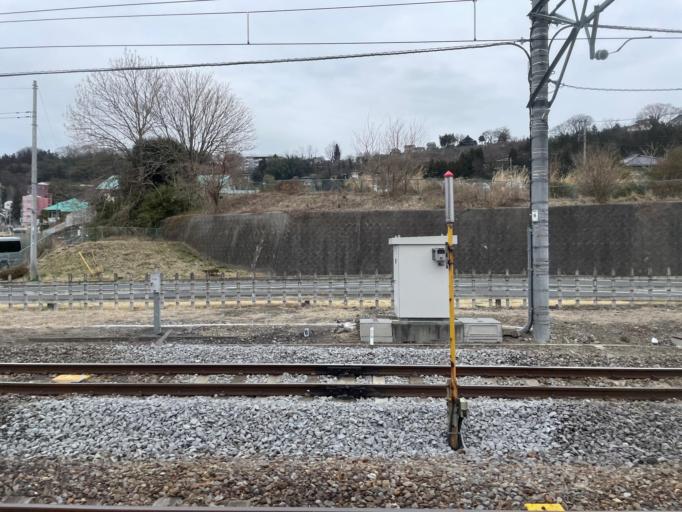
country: JP
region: Gunma
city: Numata
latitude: 36.6401
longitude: 139.0372
